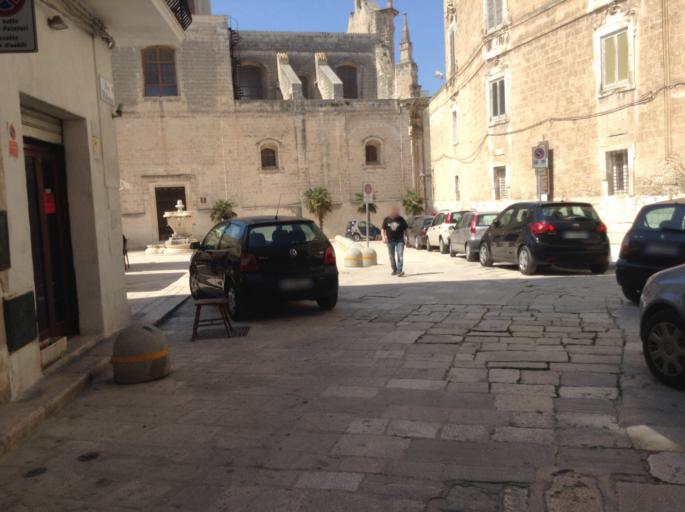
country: IT
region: Apulia
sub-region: Provincia di Bari
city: Monopoli
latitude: 40.9523
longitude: 17.3055
